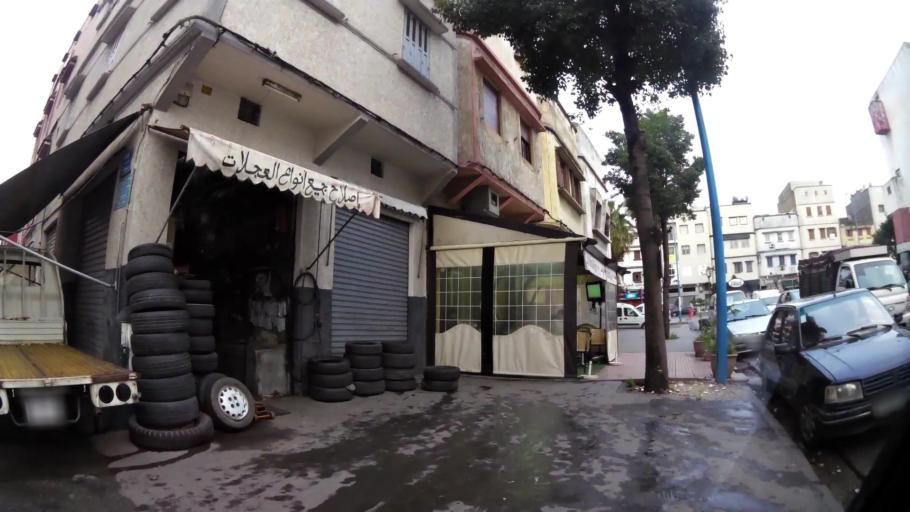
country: MA
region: Grand Casablanca
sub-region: Casablanca
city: Casablanca
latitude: 33.5536
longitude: -7.5778
